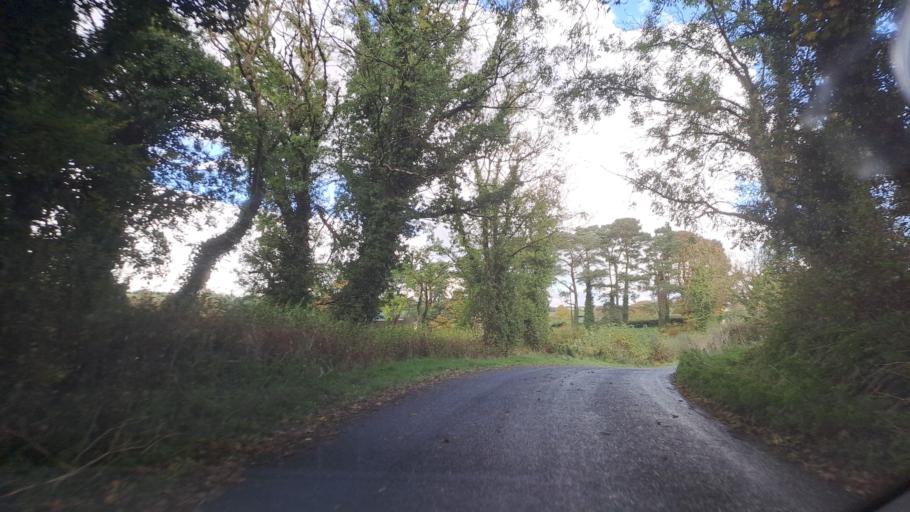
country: IE
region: Ulster
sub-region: An Cabhan
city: Bailieborough
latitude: 53.9953
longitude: -6.9735
